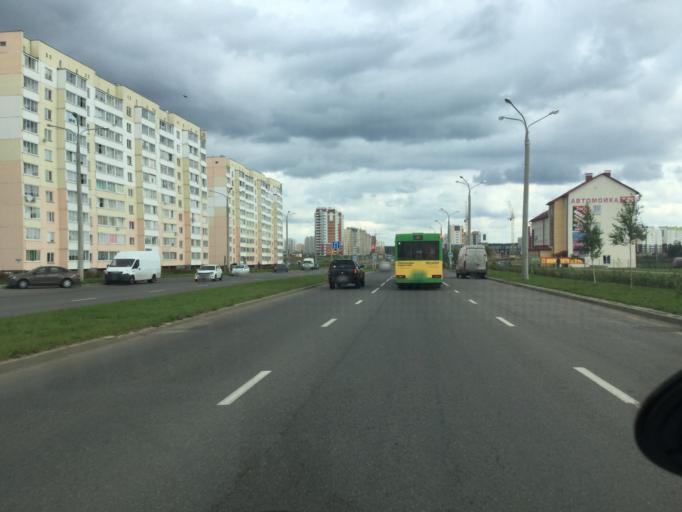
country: BY
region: Vitebsk
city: Vitebsk
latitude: 55.1659
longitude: 30.2584
